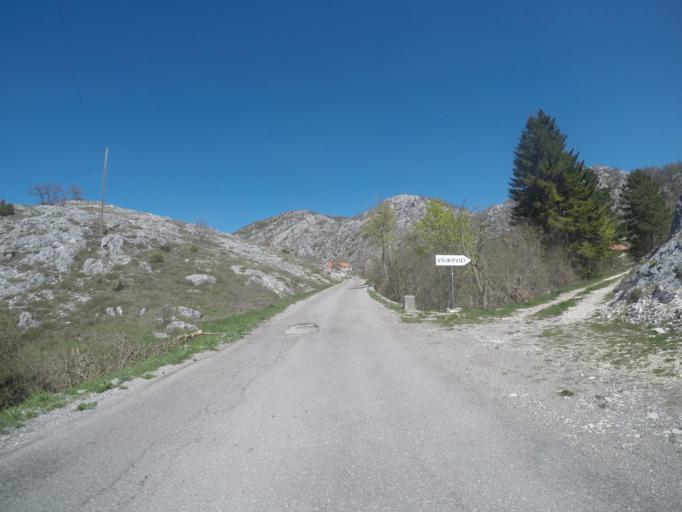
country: ME
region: Cetinje
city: Cetinje
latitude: 42.4570
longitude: 18.8736
